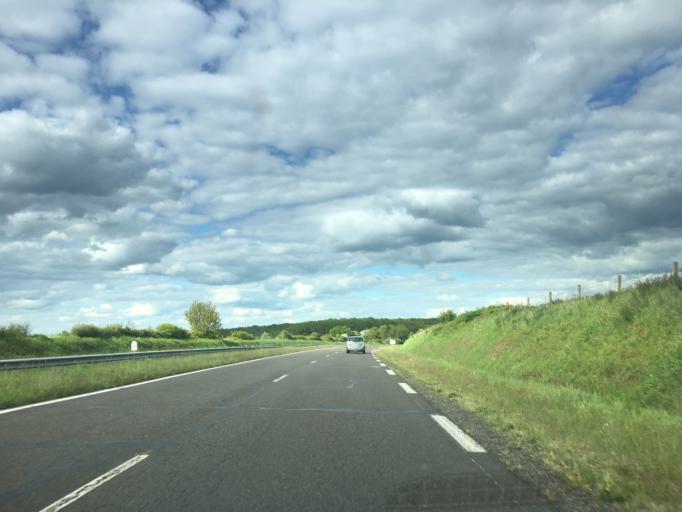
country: FR
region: Haute-Normandie
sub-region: Departement de l'Eure
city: Tillieres-sur-Avre
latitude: 48.7565
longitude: 1.0397
